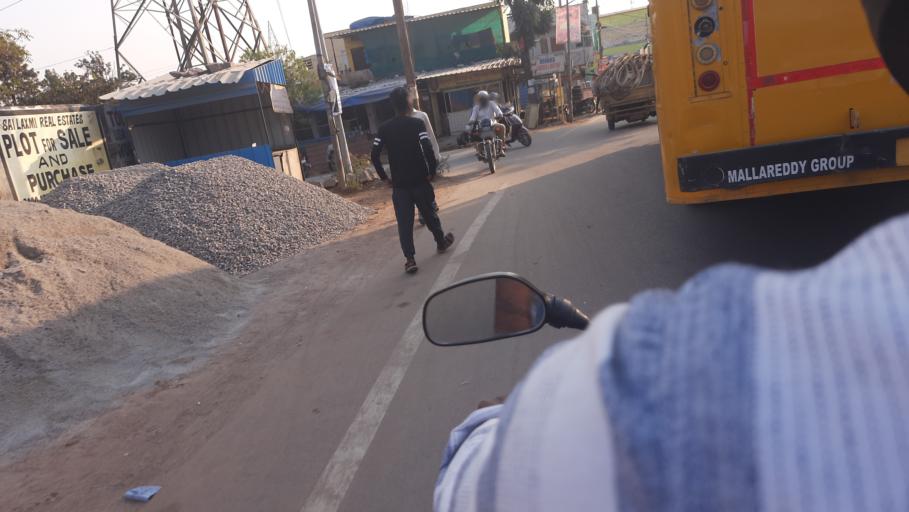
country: IN
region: Telangana
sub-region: Rangareddi
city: Secunderabad
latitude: 17.5015
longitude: 78.5390
